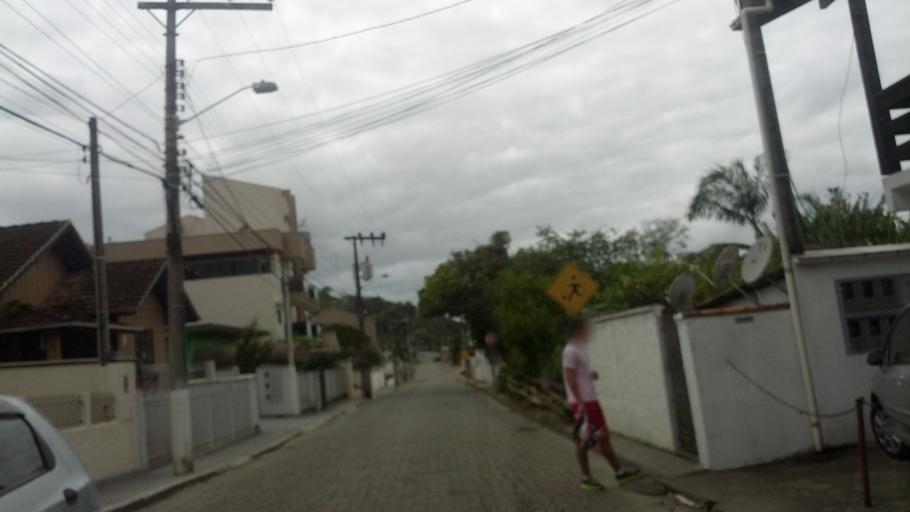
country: BR
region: Santa Catarina
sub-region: Blumenau
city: Blumenau
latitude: -26.9110
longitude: -49.1133
